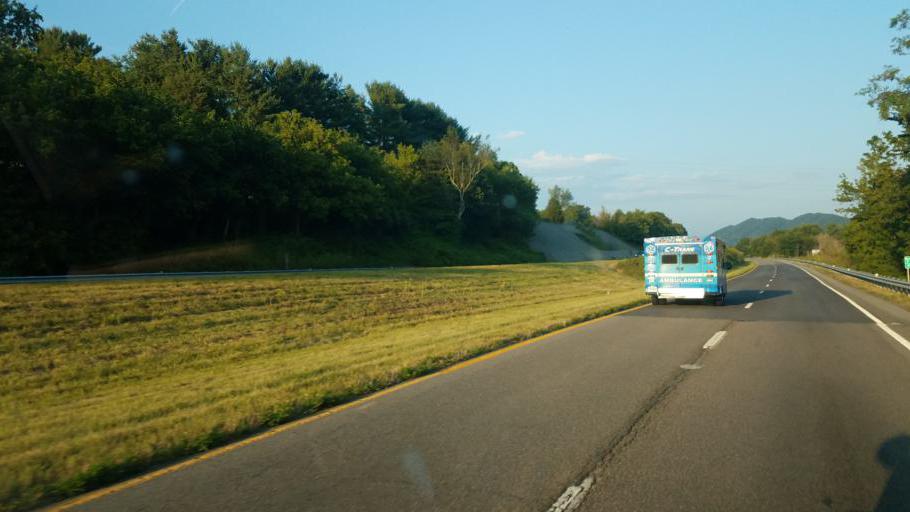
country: US
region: Virginia
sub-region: Scott County
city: Gate City
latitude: 36.6340
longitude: -82.6259
